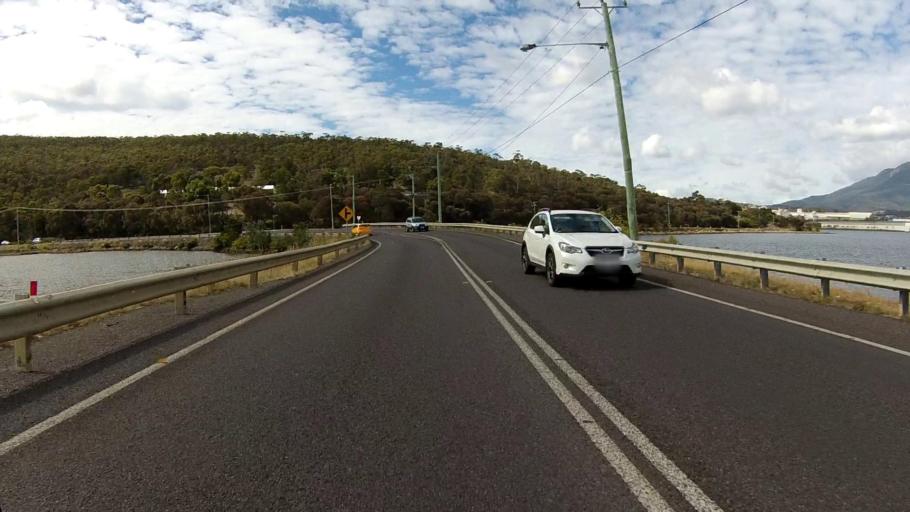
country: AU
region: Tasmania
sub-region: Glenorchy
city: Lutana
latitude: -42.8172
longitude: 147.3204
